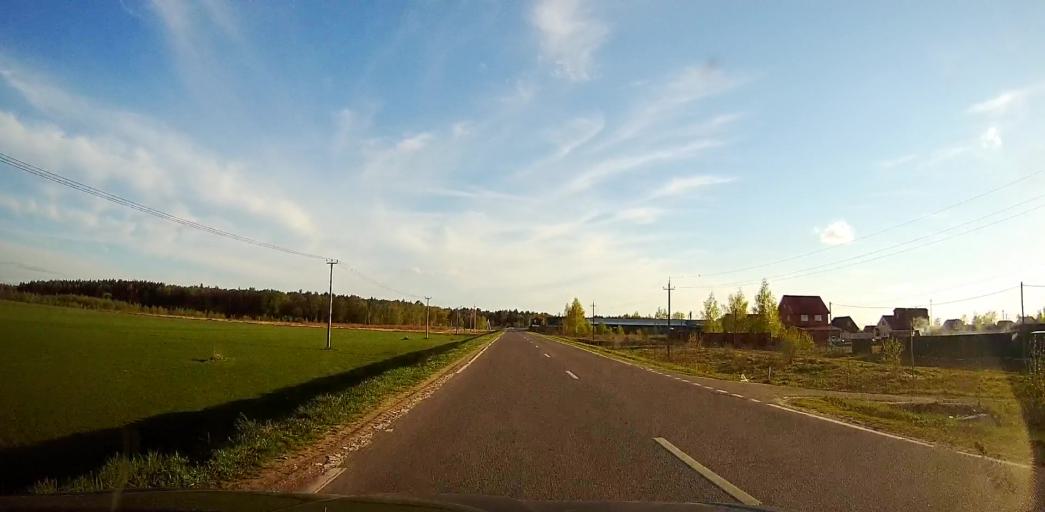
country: RU
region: Moskovskaya
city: Malino
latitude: 55.2797
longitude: 38.1708
